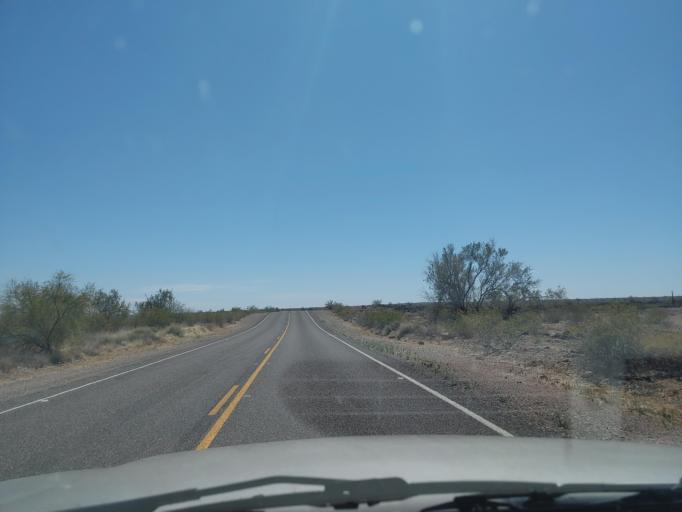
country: US
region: Arizona
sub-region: Maricopa County
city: Gila Bend
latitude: 32.9189
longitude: -113.2833
